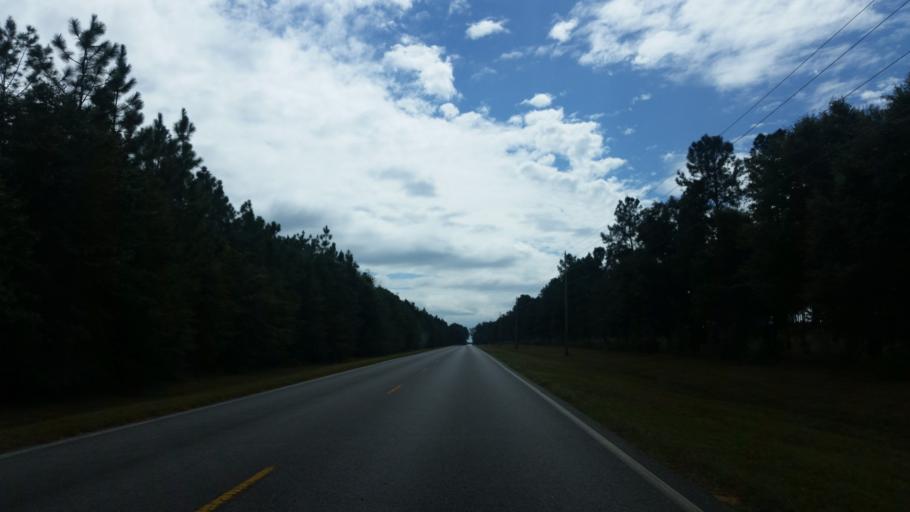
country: US
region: Florida
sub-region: Santa Rosa County
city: Point Baker
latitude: 30.7897
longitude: -86.9404
